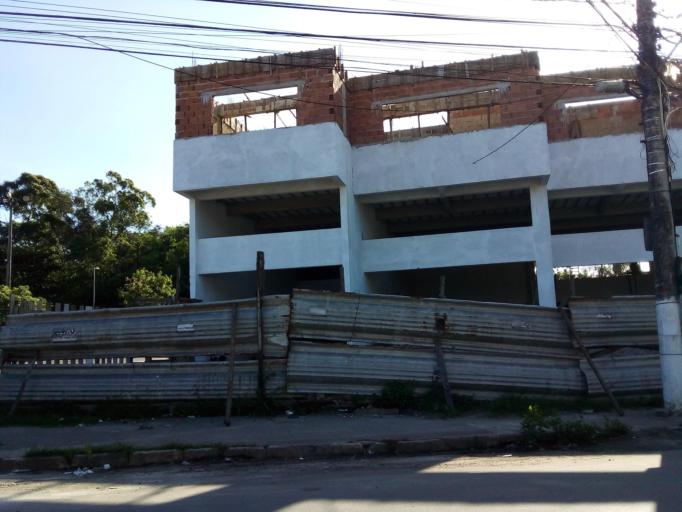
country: BR
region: Espirito Santo
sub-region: Vitoria
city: Vitoria
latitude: -20.3114
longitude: -40.3696
